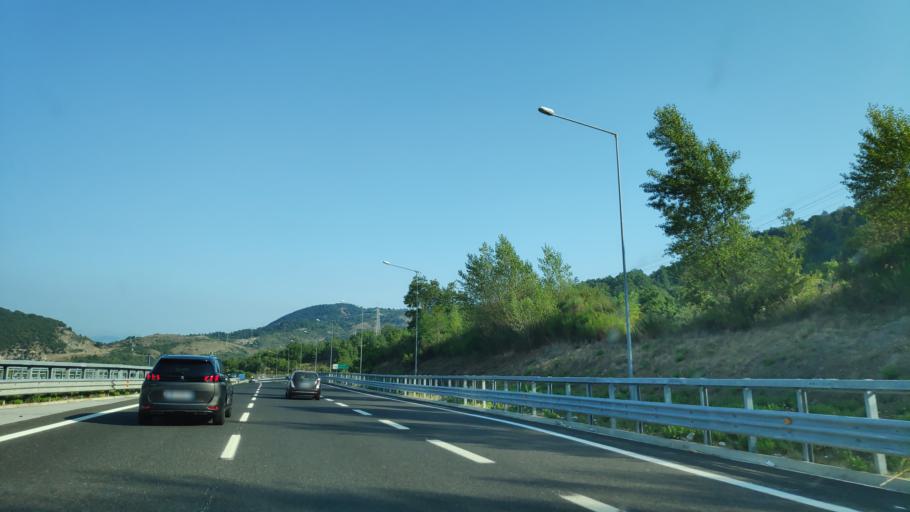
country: IT
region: Basilicate
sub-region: Provincia di Potenza
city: Lagonegro
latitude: 40.1501
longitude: 15.7506
